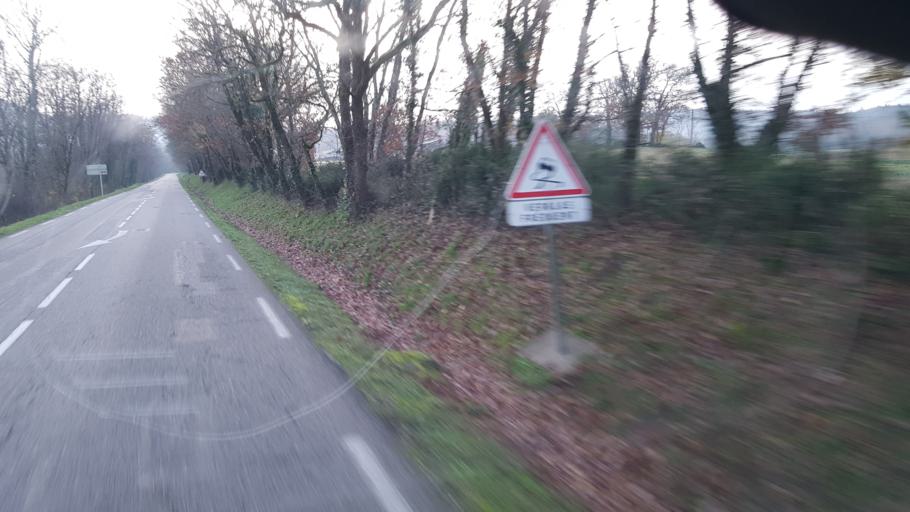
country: FR
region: Midi-Pyrenees
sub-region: Departement du Tarn-et-Garonne
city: Montricoux
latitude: 44.0697
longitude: 1.6514
